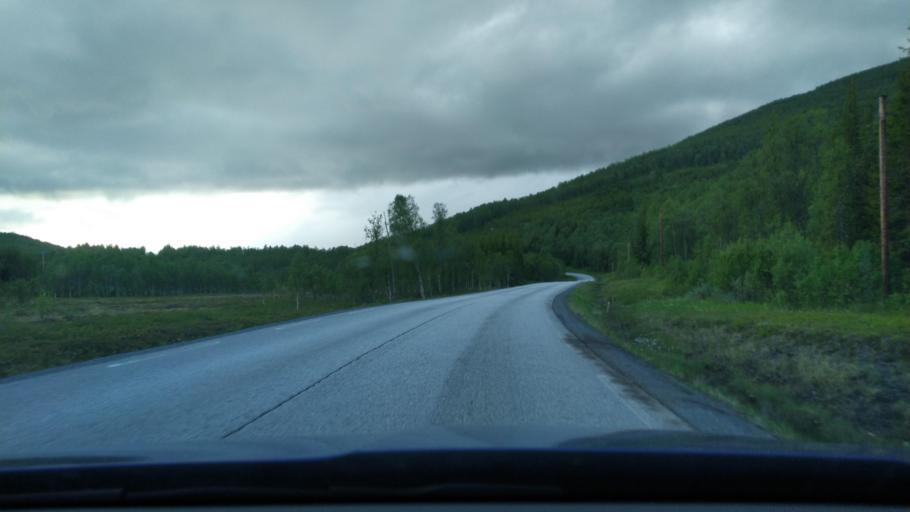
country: NO
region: Troms
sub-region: Dyroy
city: Brostadbotn
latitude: 69.0563
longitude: 17.7852
